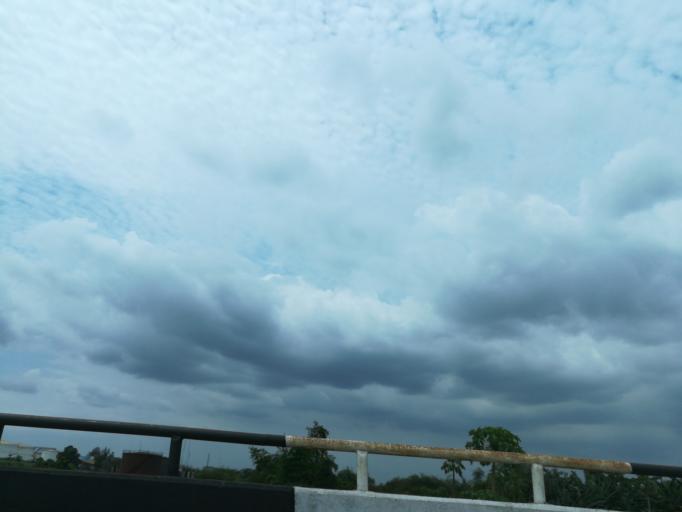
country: NG
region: Lagos
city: Oshodi
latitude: 6.5598
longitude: 3.3253
